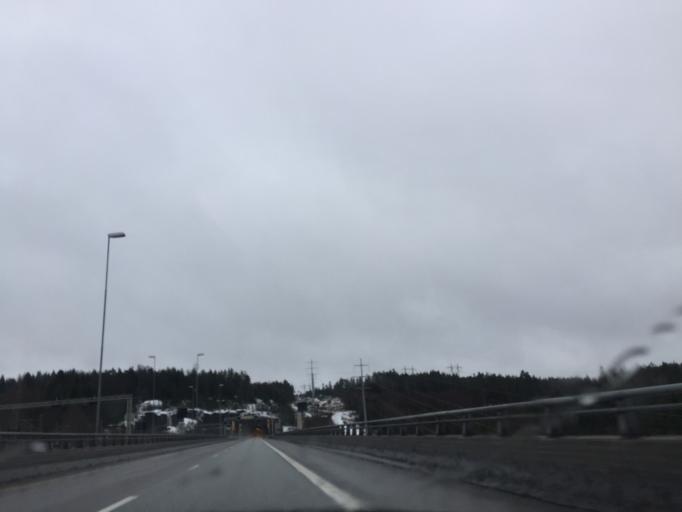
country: NO
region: Akershus
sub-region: Vestby
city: Vestby
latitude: 59.5386
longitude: 10.7266
